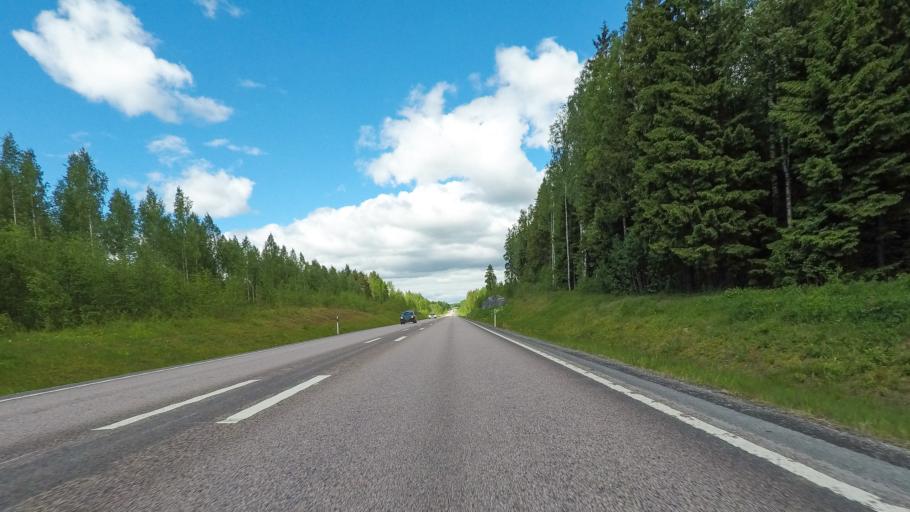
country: FI
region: Paijanne Tavastia
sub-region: Lahti
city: Heinola
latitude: 61.3926
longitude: 26.0510
